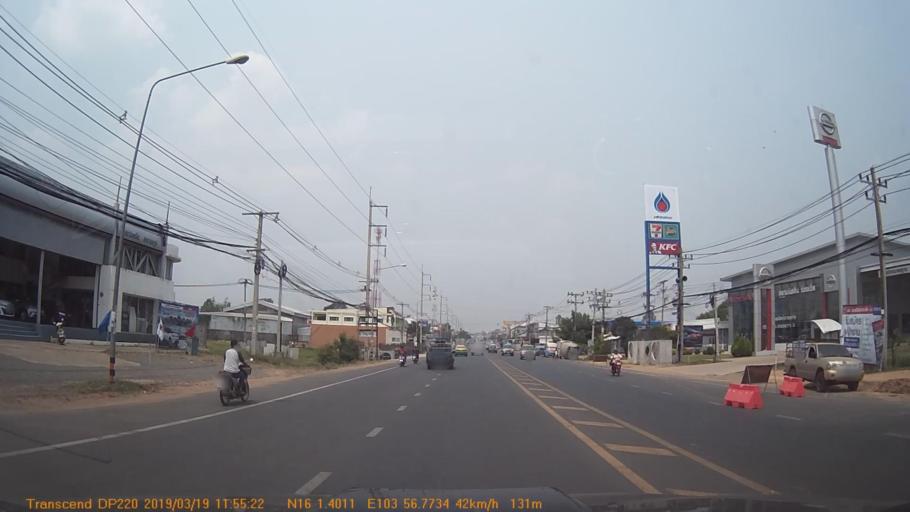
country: TH
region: Roi Et
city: Ban Selaphum
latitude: 16.0234
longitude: 103.9461
